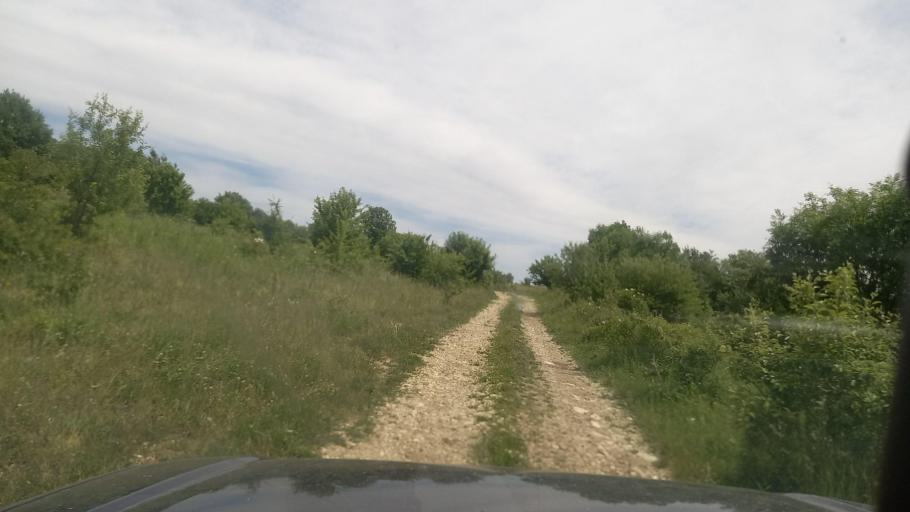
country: RU
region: Karachayevo-Cherkesiya
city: Pregradnaya
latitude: 44.0907
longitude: 41.1587
